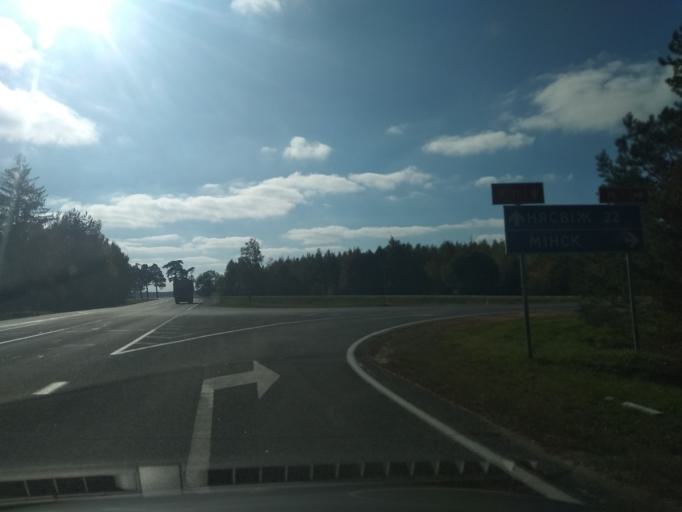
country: BY
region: Minsk
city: Haradzyeya
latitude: 53.3771
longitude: 26.5098
